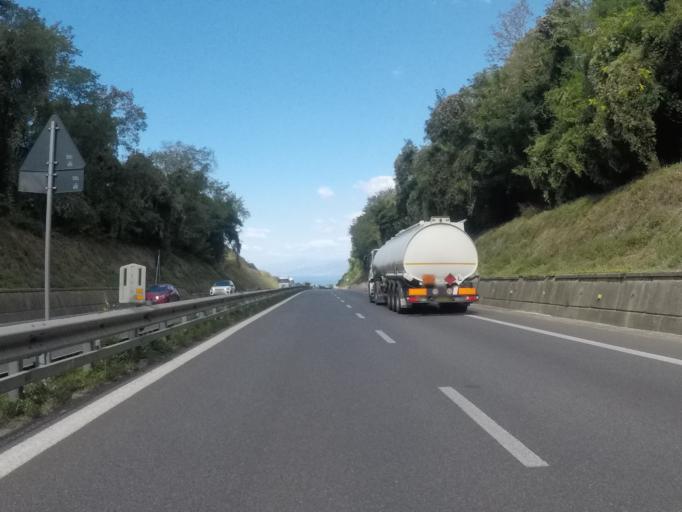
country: IT
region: Calabria
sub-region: Provincia di Vibo-Valentia
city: Sant'Onofrio
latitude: 38.7091
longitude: 16.1539
